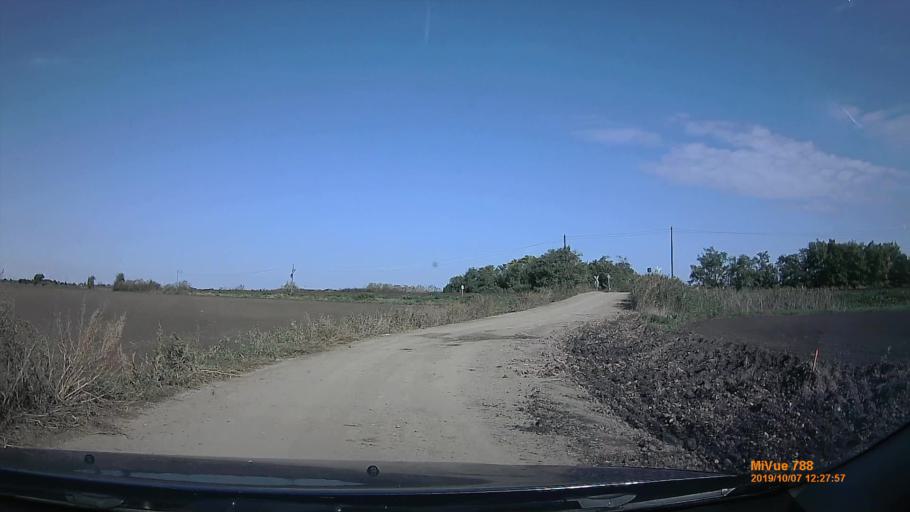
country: HU
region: Jasz-Nagykun-Szolnok
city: Kunszentmarton
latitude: 46.8709
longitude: 20.2733
